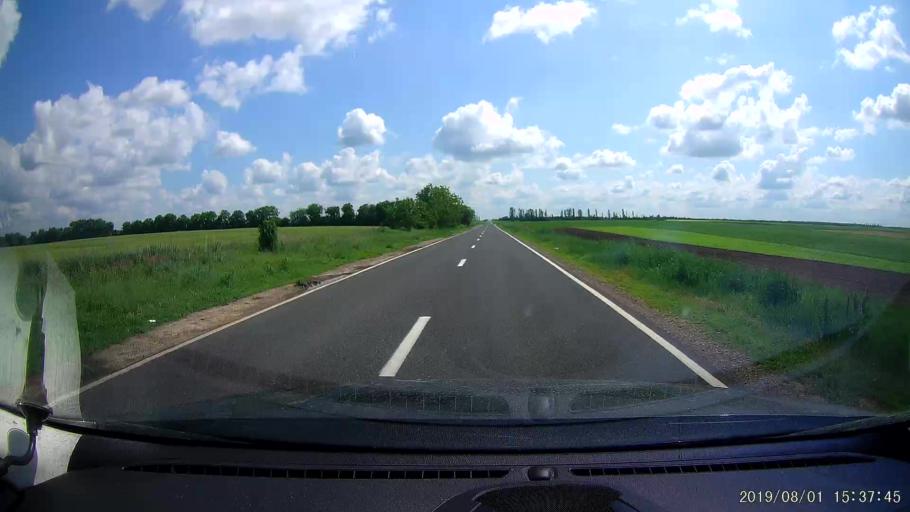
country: RO
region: Braila
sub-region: Comuna Insuratei
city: Insuratei
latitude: 44.8975
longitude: 27.5857
